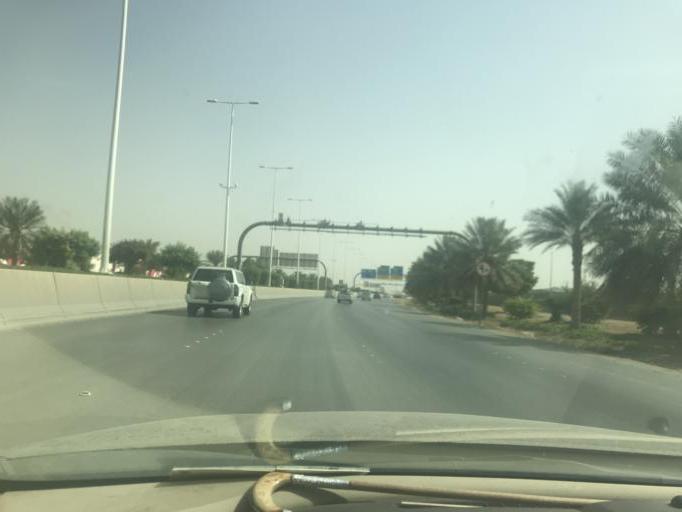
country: SA
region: Ar Riyad
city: Riyadh
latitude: 24.7329
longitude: 46.7089
